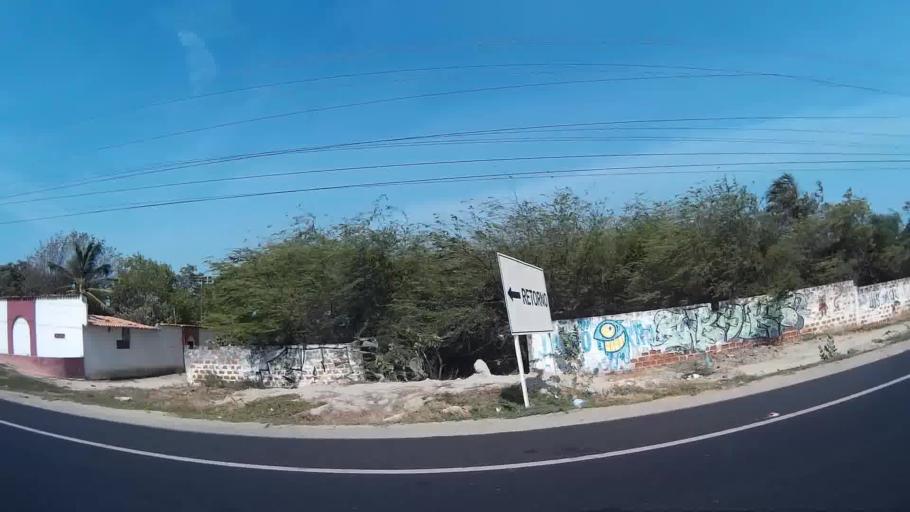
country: CO
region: Magdalena
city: Santa Marta
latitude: 11.1576
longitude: -74.2235
